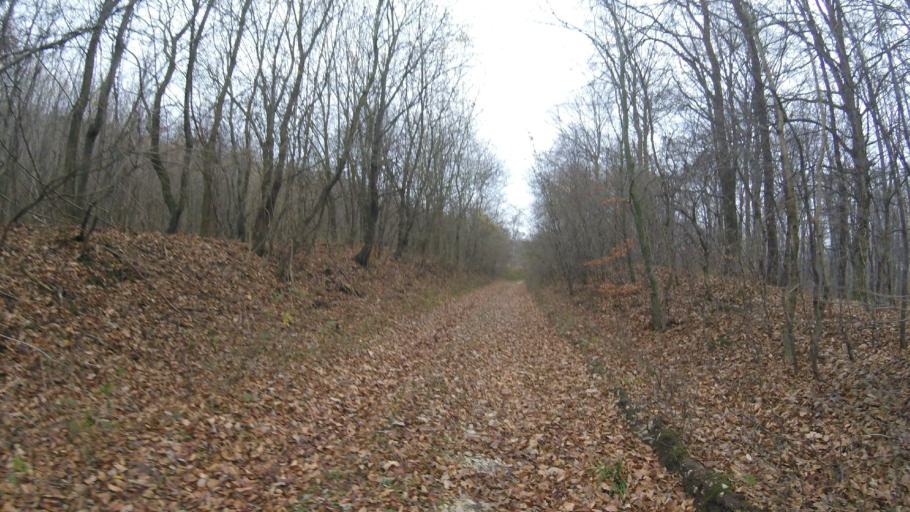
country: HU
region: Komarom-Esztergom
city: Tardos
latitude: 47.6735
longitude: 18.4657
